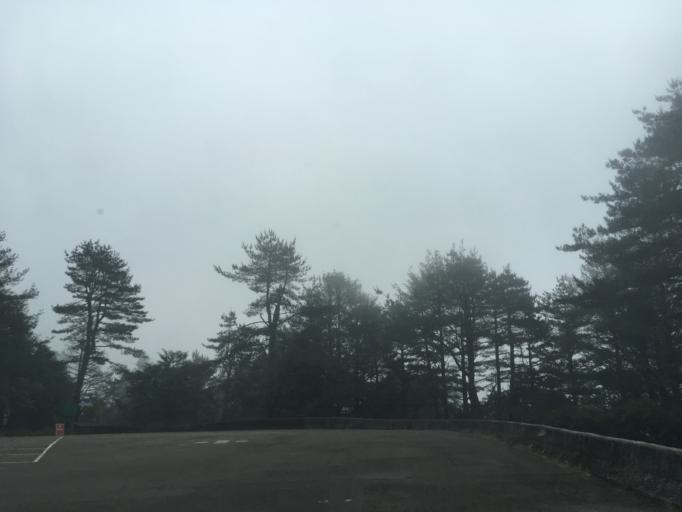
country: TW
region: Taiwan
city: Fengyuan
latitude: 24.2826
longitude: 121.0290
